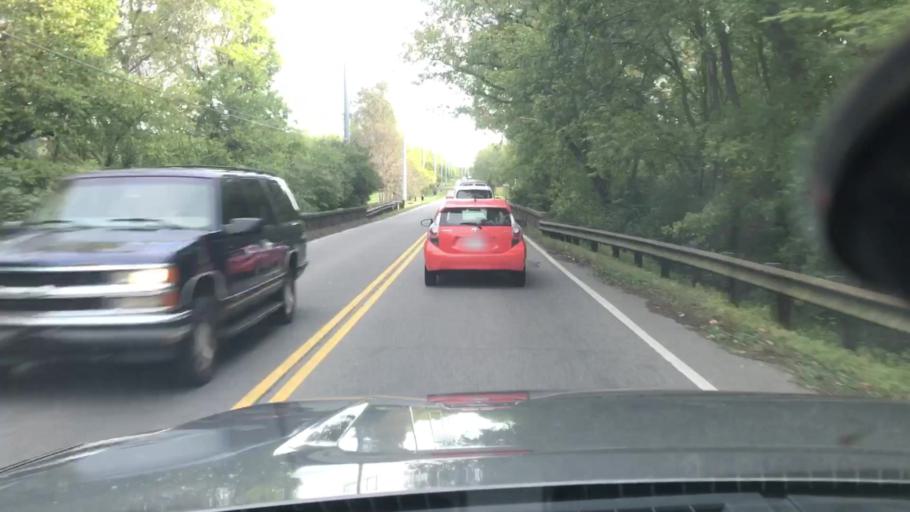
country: US
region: Tennessee
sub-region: Davidson County
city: Forest Hills
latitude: 36.0525
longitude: -86.8585
